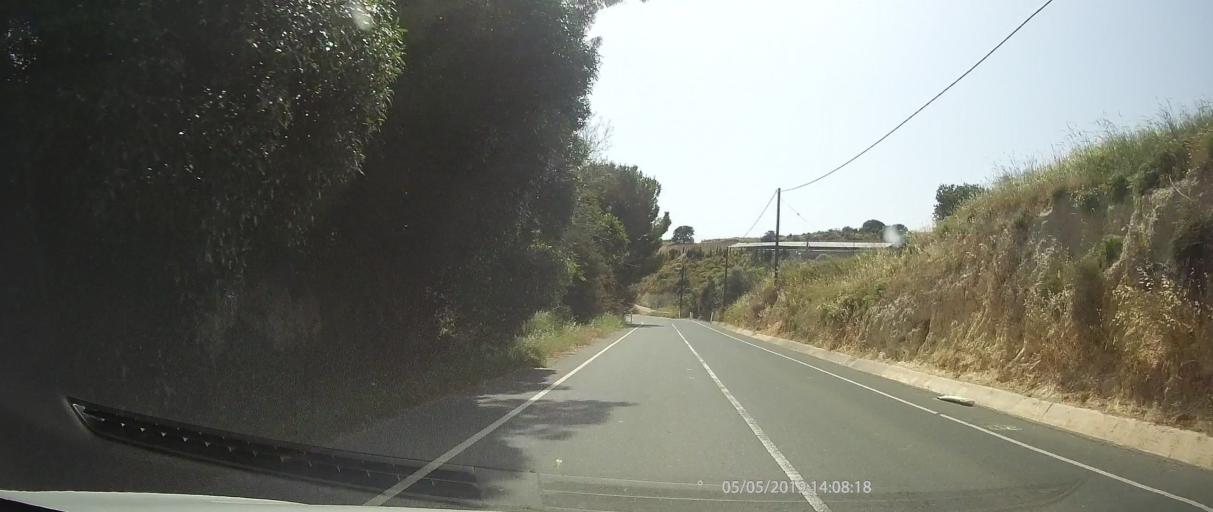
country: CY
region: Limassol
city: Pissouri
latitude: 34.7328
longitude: 32.5850
